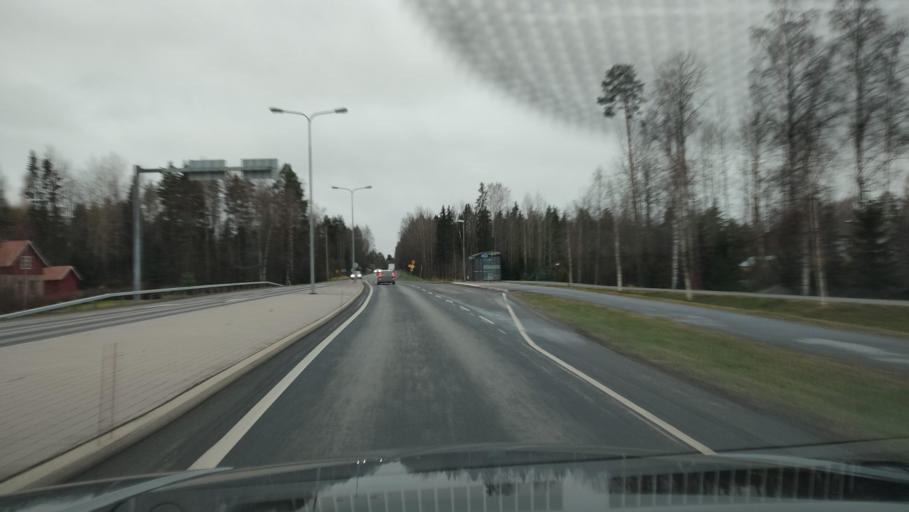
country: FI
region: Southern Ostrobothnia
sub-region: Seinaejoki
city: Ilmajoki
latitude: 62.7702
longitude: 22.6804
